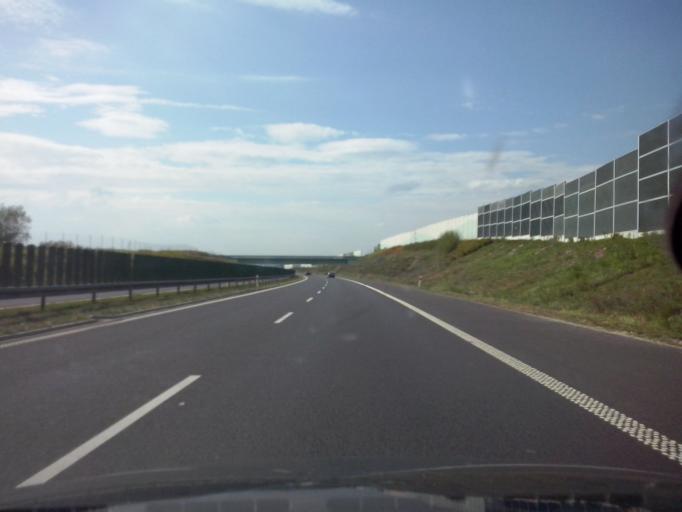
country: PL
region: Lesser Poland Voivodeship
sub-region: Powiat tarnowski
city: Lukowa
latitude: 50.0633
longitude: 20.9834
